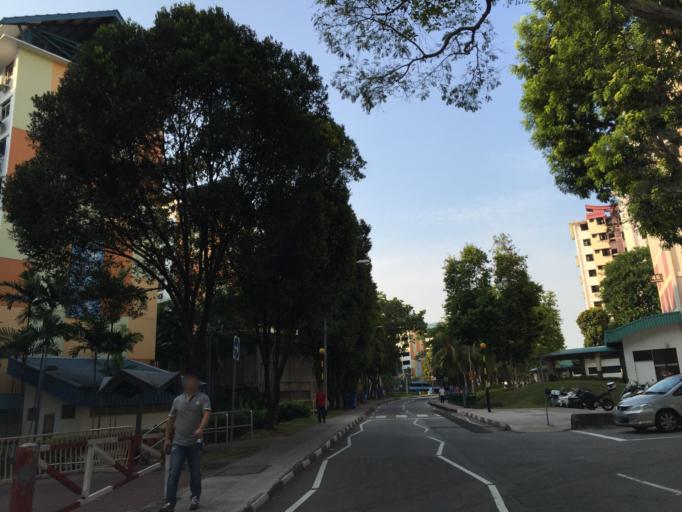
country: SG
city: Singapore
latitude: 1.2997
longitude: 103.7988
